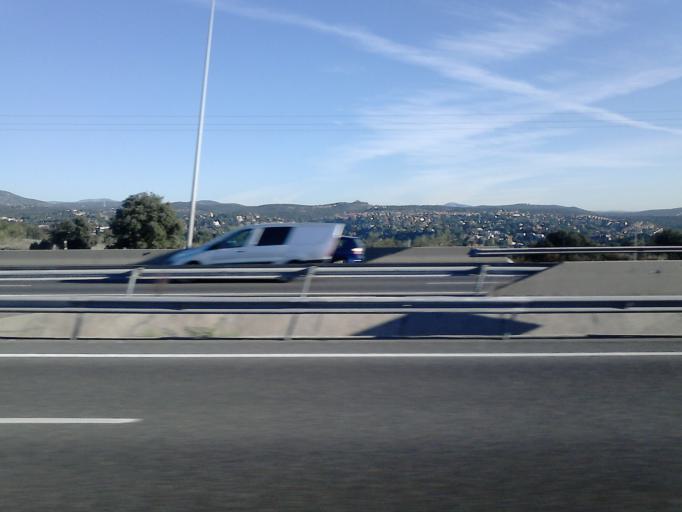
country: ES
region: Madrid
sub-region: Provincia de Madrid
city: Las Matas
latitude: 40.5643
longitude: -3.9081
